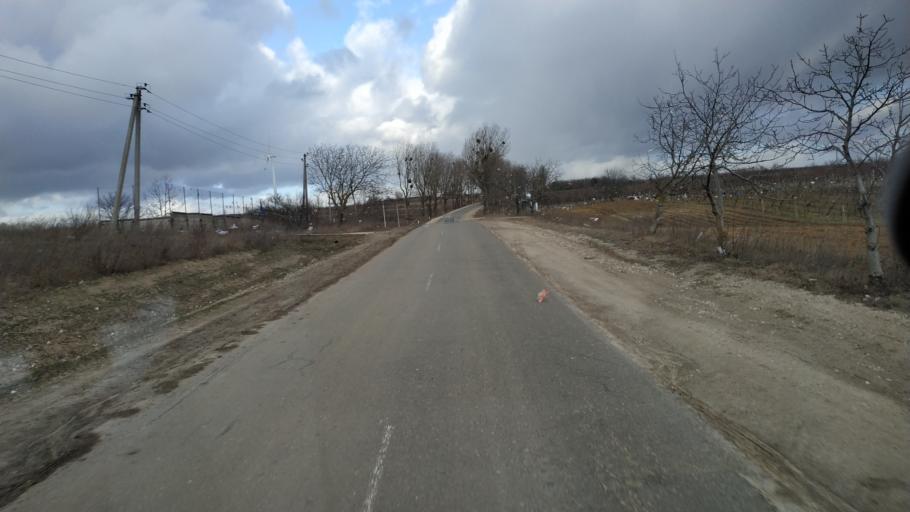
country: MD
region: Calarasi
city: Calarasi
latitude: 47.2827
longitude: 28.3327
